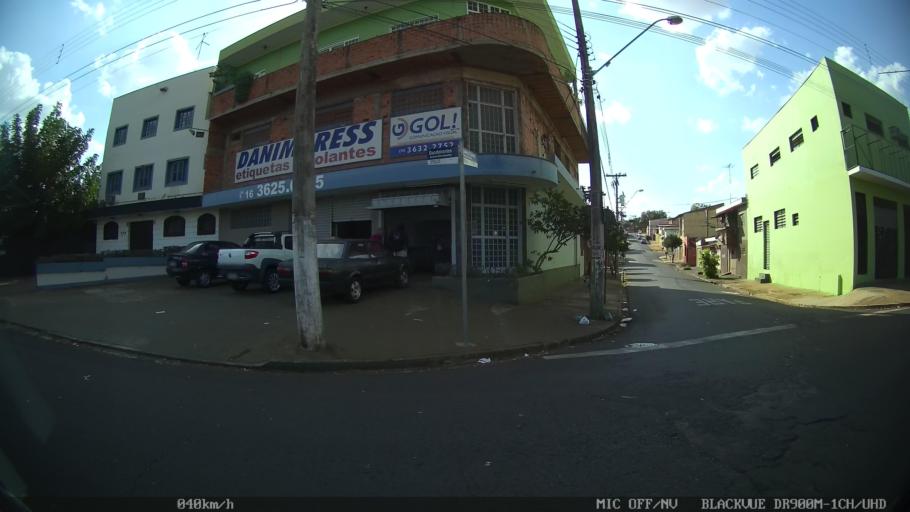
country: BR
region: Sao Paulo
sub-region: Ribeirao Preto
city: Ribeirao Preto
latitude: -21.1766
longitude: -47.8224
